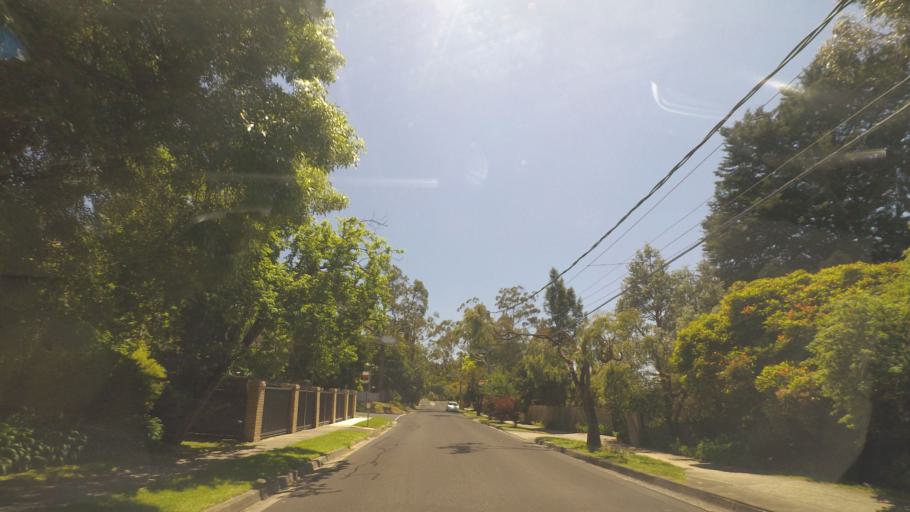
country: AU
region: Victoria
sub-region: Maroondah
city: Croydon North
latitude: -37.7764
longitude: 145.2849
